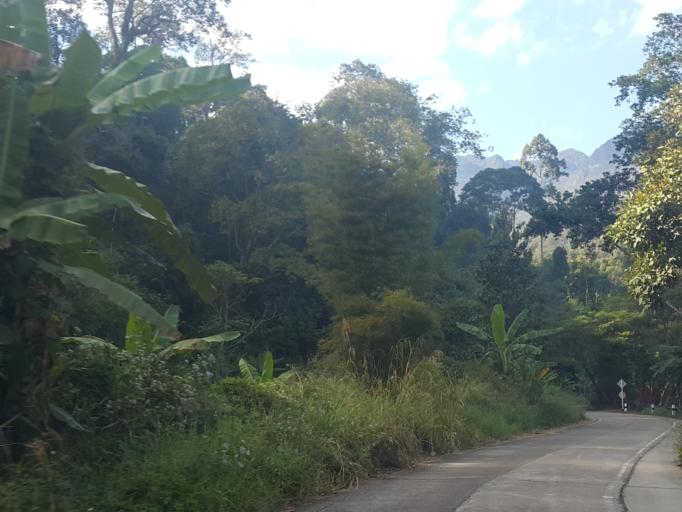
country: TH
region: Chiang Mai
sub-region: Amphoe Chiang Dao
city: Chiang Dao
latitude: 19.4103
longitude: 98.9225
